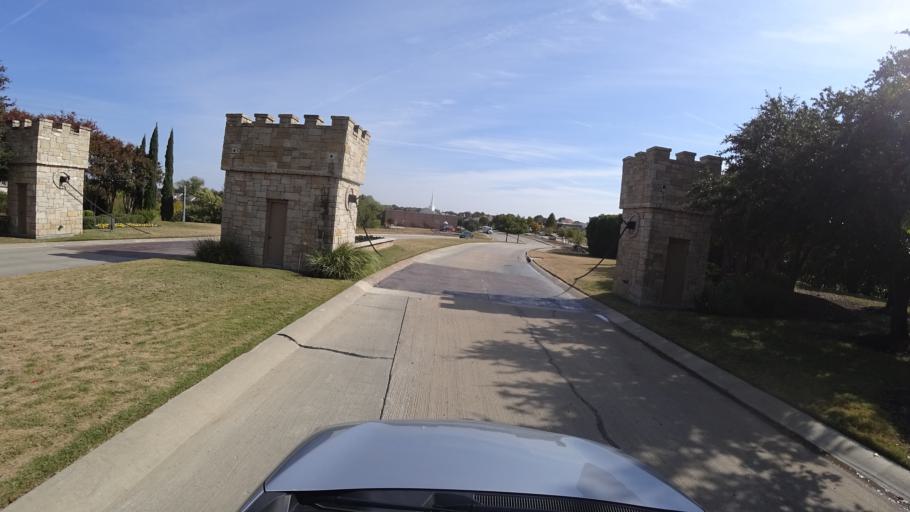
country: US
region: Texas
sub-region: Denton County
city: The Colony
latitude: 33.0363
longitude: -96.8875
